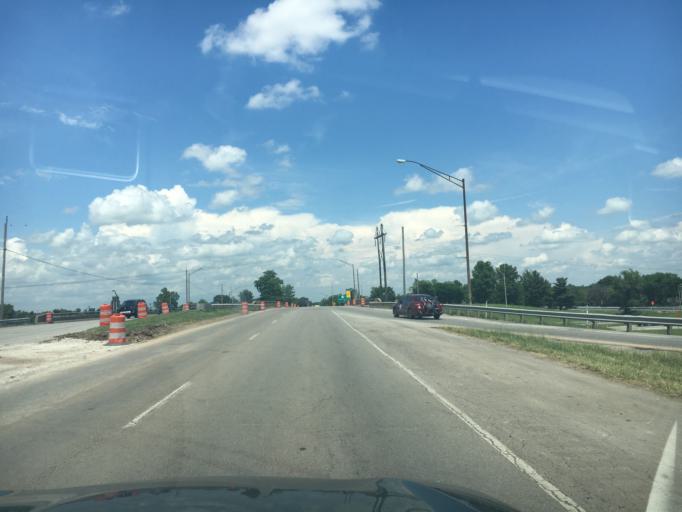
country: US
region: Kentucky
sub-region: Fayette County
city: Lexington-Fayette
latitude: 38.0735
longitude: -84.4955
